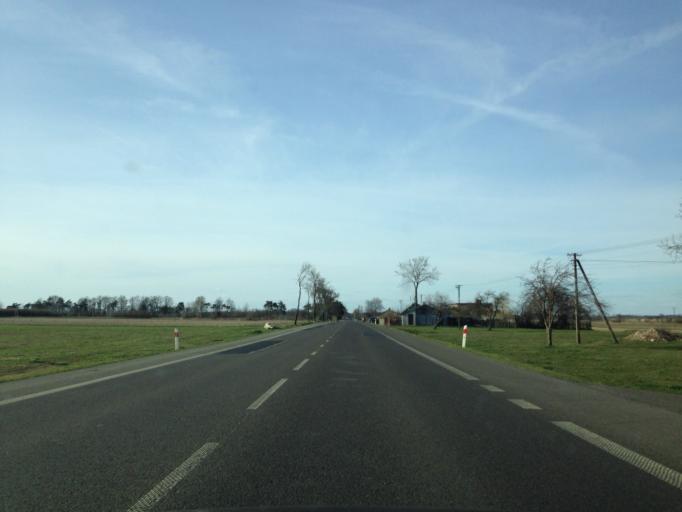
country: PL
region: Lodz Voivodeship
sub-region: Powiat kutnowski
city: Ostrowy
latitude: 52.3268
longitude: 19.1514
